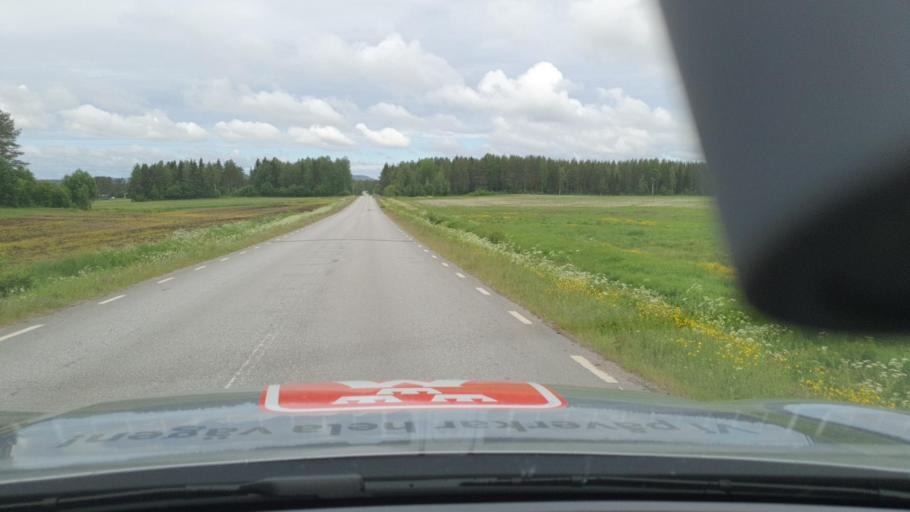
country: SE
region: Norrbotten
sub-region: Lulea Kommun
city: Ranea
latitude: 65.9528
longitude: 22.1229
